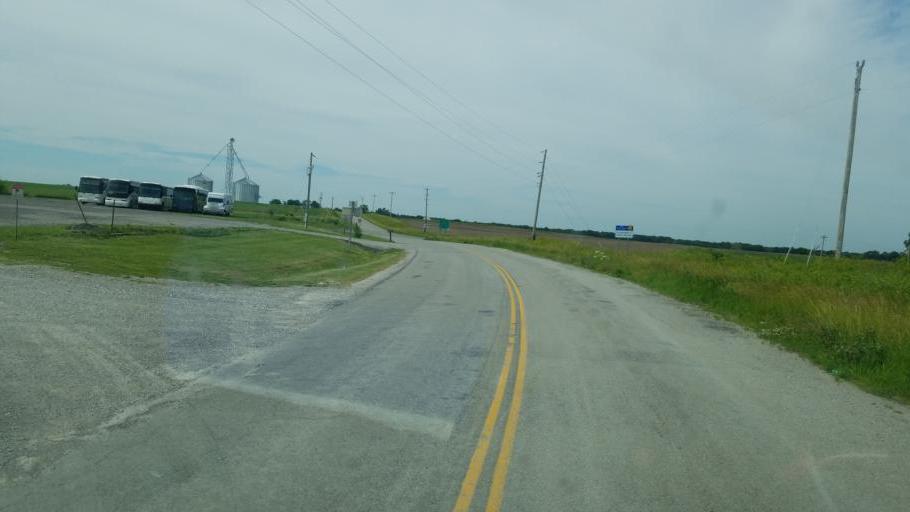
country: US
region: Missouri
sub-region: Saline County
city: Marshall
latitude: 38.9551
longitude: -93.0870
